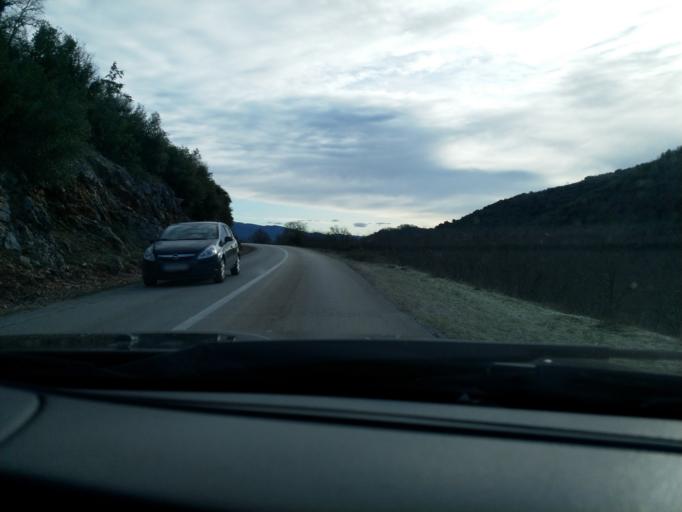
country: GR
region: Epirus
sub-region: Nomos Ioanninon
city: Asprangeloi
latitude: 39.8672
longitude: 20.7328
